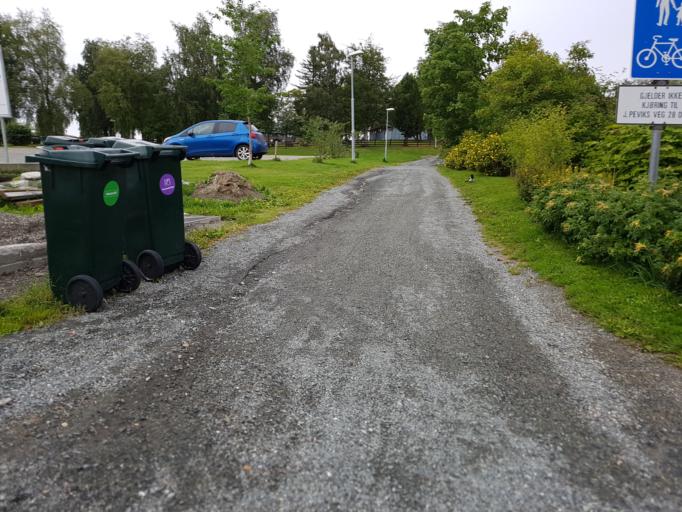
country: NO
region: Sor-Trondelag
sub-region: Trondheim
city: Trondheim
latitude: 63.4033
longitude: 10.3719
